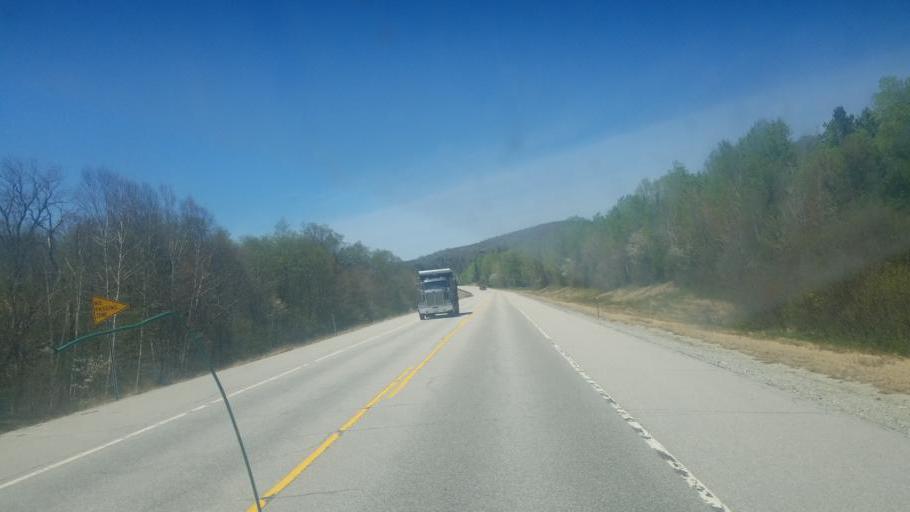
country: US
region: New Hampshire
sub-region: Grafton County
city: Deerfield
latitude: 44.2687
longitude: -71.5052
